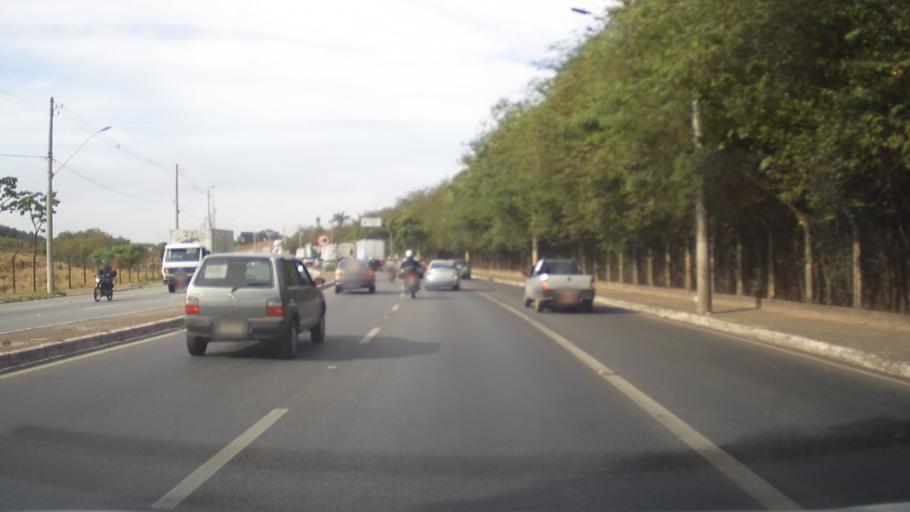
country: BR
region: Minas Gerais
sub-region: Contagem
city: Contagem
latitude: -19.8981
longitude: -44.0440
